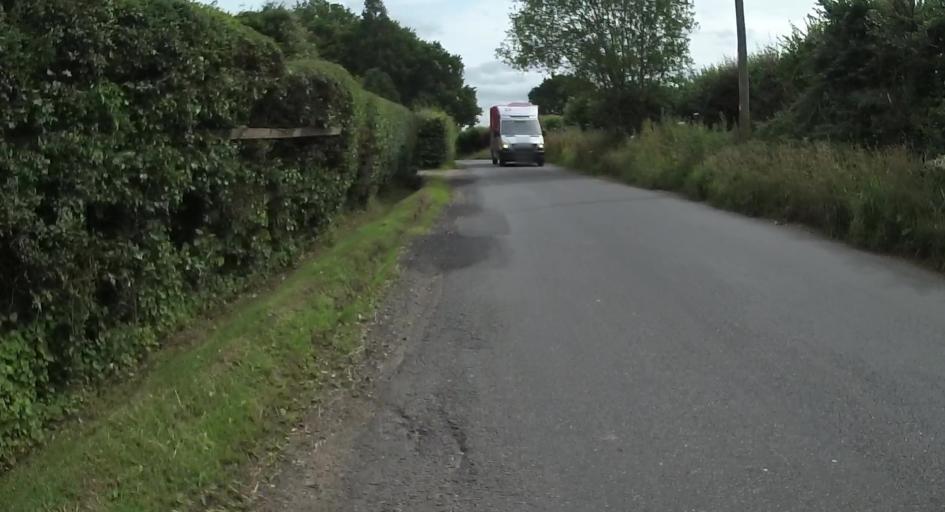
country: GB
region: England
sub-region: West Berkshire
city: Stratfield Mortimer
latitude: 51.3431
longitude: -1.0424
